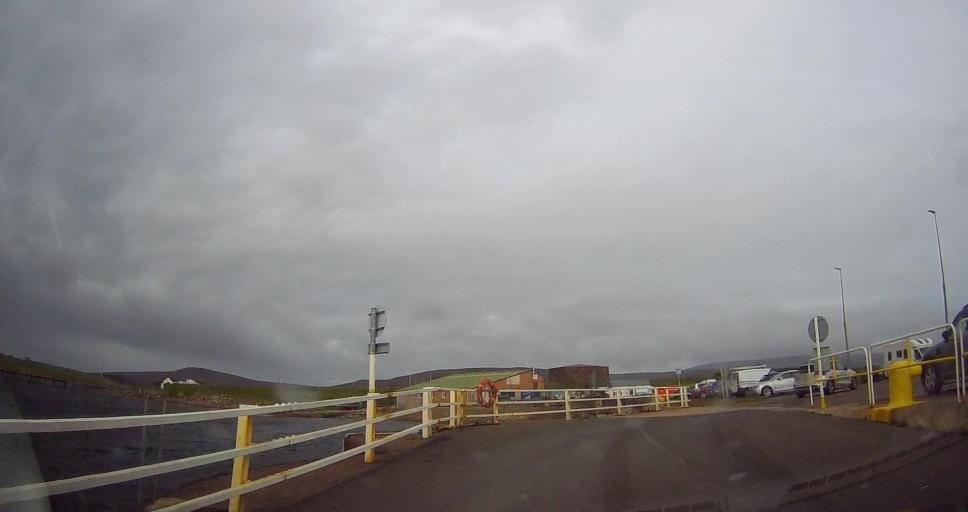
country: GB
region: Scotland
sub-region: Orkney Islands
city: Stromness
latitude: 58.8335
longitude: -3.1920
